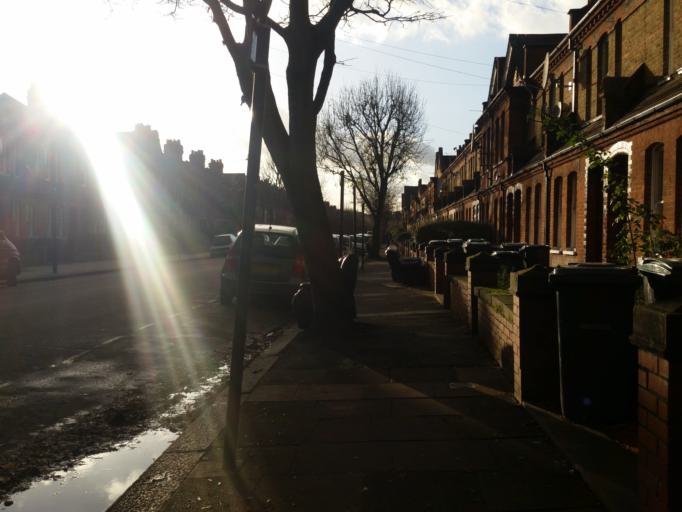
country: GB
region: England
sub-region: Greater London
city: Harringay
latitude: 51.5981
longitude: -0.0968
